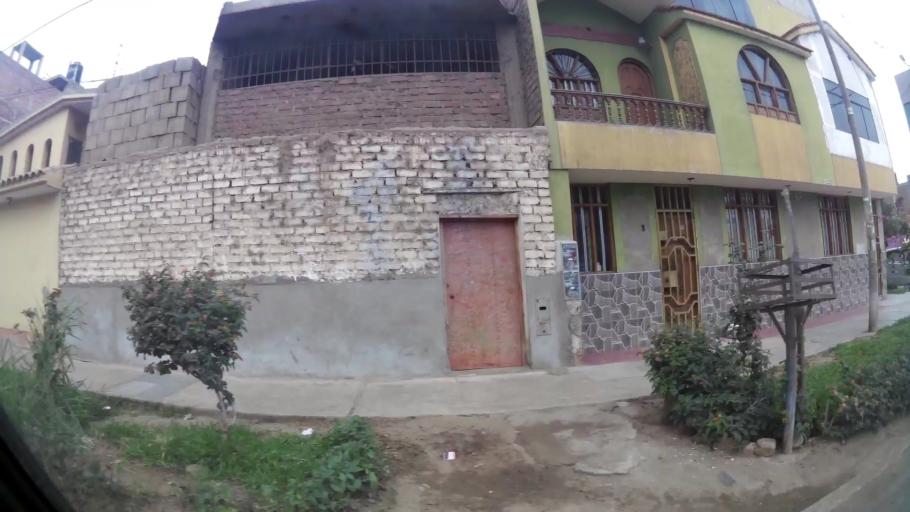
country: PE
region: La Libertad
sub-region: Provincia de Trujillo
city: Trujillo
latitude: -8.0993
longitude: -79.0216
